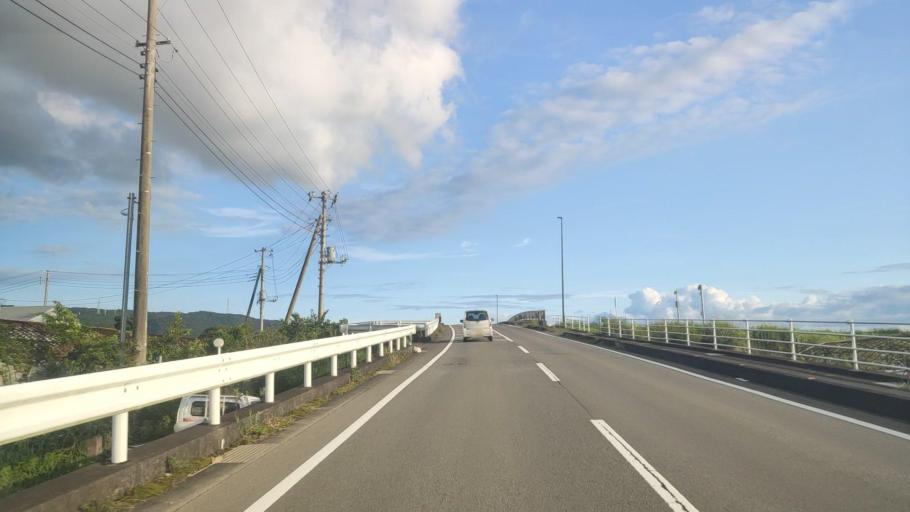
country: JP
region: Shizuoka
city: Mishima
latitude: 35.0735
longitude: 138.9493
